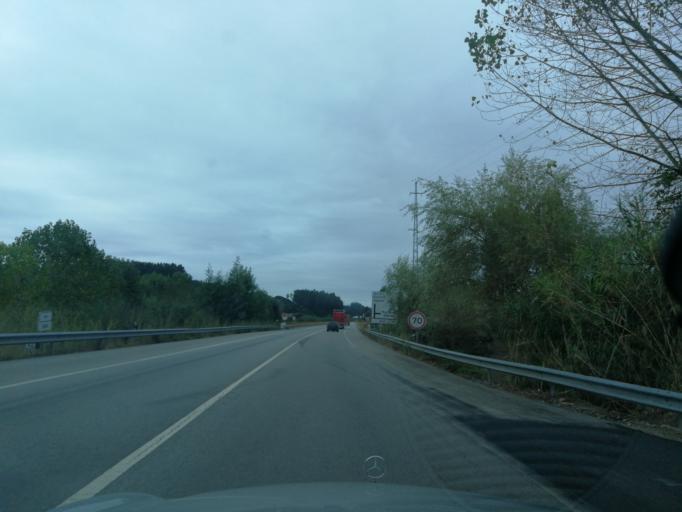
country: PT
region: Aveiro
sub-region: Agueda
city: Valongo
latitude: 40.6445
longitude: -8.4664
